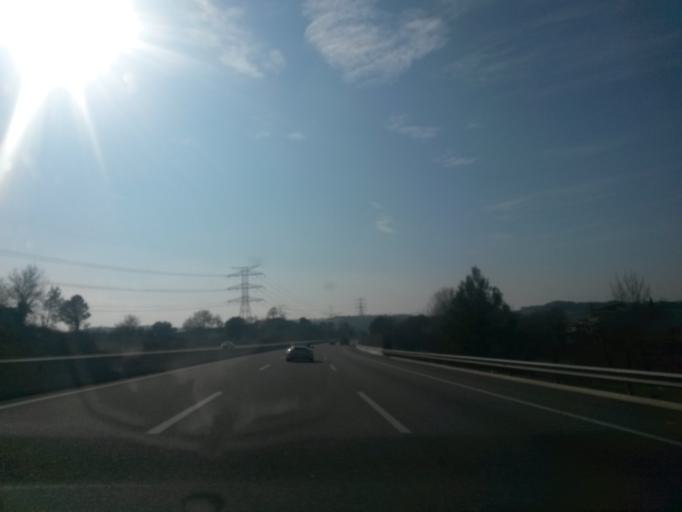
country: ES
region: Catalonia
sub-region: Provincia de Girona
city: Viladasens
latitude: 42.1076
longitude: 2.9111
